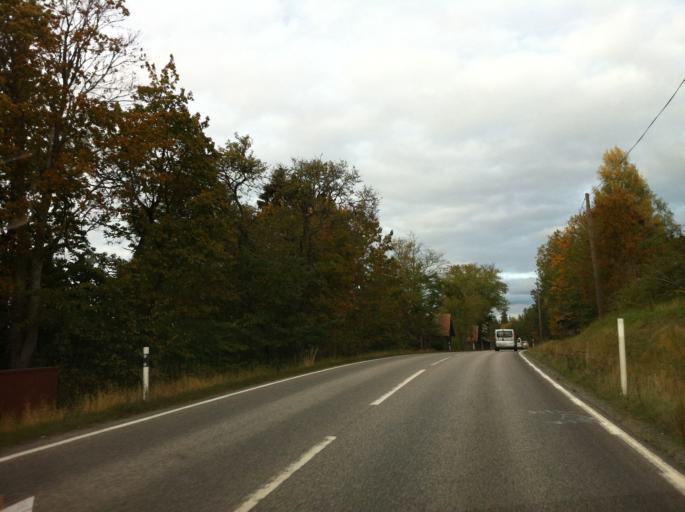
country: SE
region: OEstergoetland
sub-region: Motala Kommun
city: Ryd
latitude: 58.6869
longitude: 14.9648
